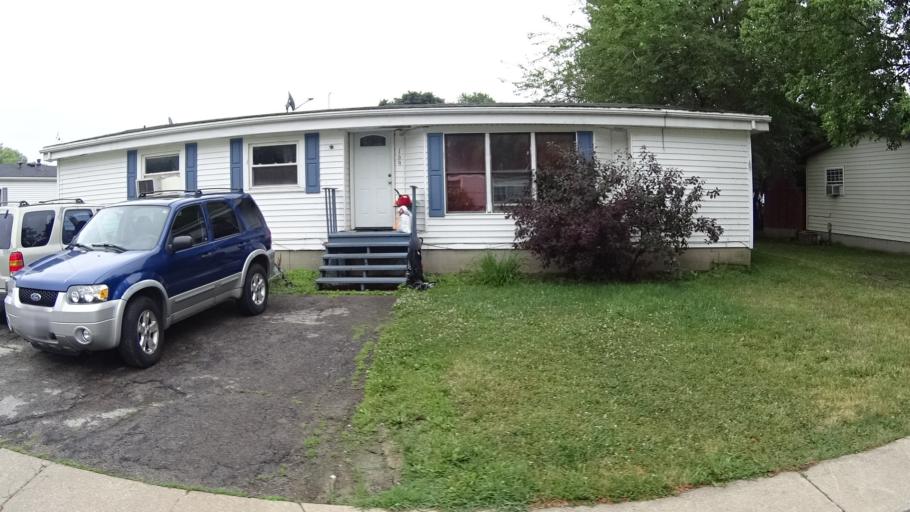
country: US
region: Ohio
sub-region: Erie County
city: Sandusky
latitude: 41.4408
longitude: -82.6681
